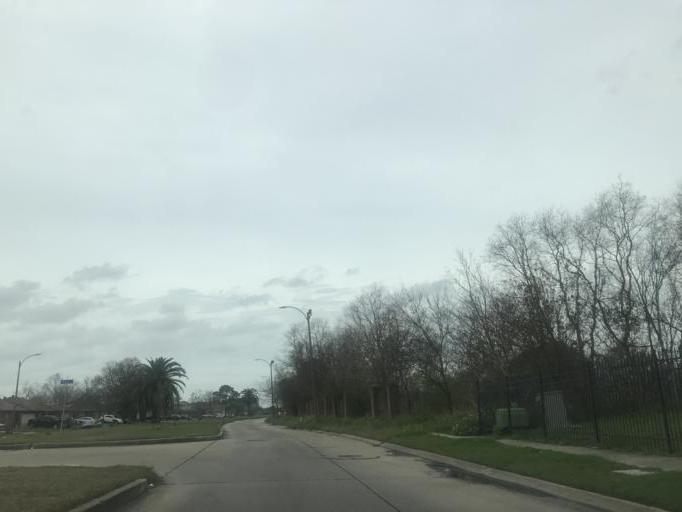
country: US
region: Louisiana
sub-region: Saint Bernard Parish
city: Arabi
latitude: 30.0256
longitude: -89.9803
